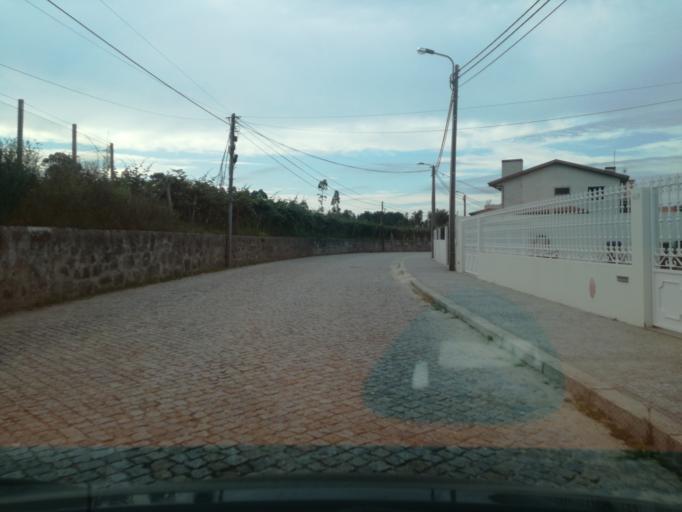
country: PT
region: Porto
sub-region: Maia
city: Maia
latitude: 41.2496
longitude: -8.6093
